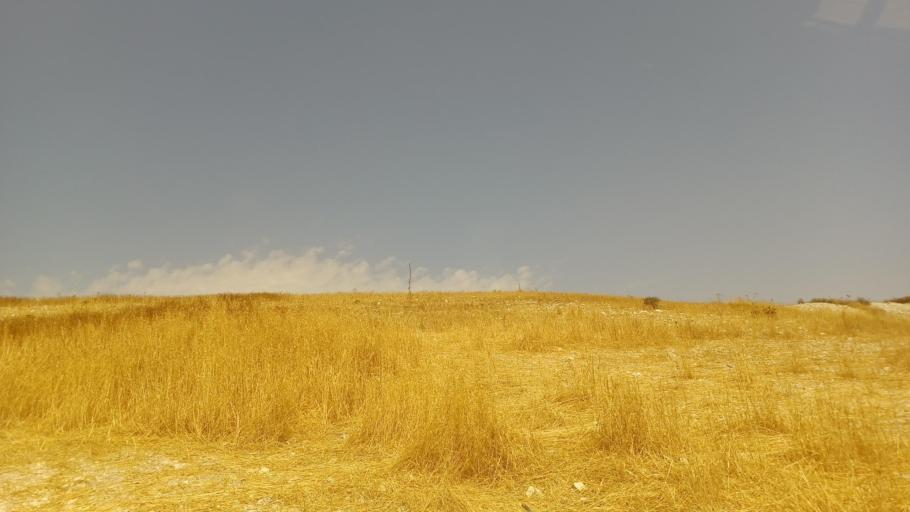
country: CY
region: Larnaka
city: Troulloi
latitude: 35.0318
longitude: 33.5983
